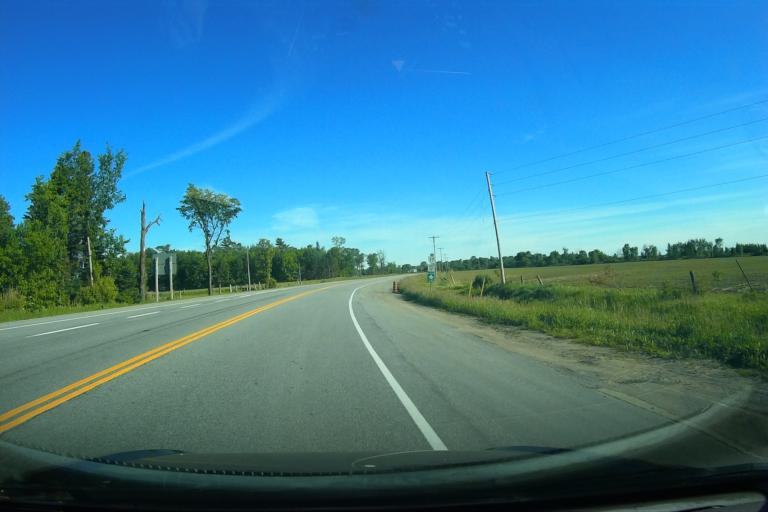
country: CA
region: Quebec
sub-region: Outaouais
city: Fort-Coulonge
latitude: 45.6462
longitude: -76.9015
